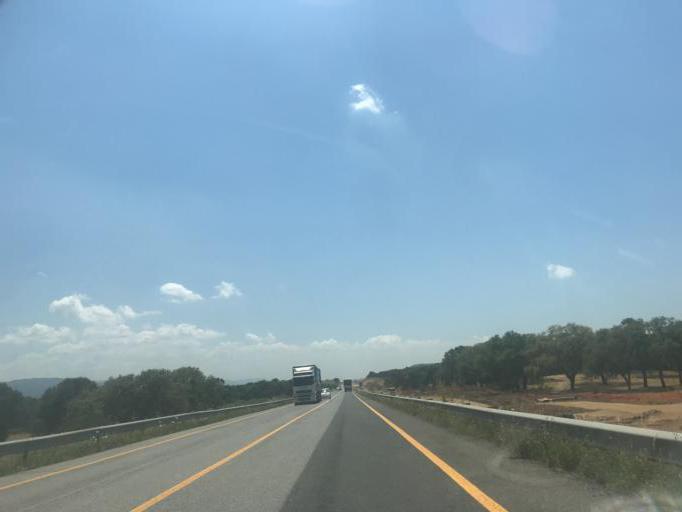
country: IT
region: Sardinia
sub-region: Provincia di Olbia-Tempio
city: Monti
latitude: 40.7922
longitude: 9.2644
